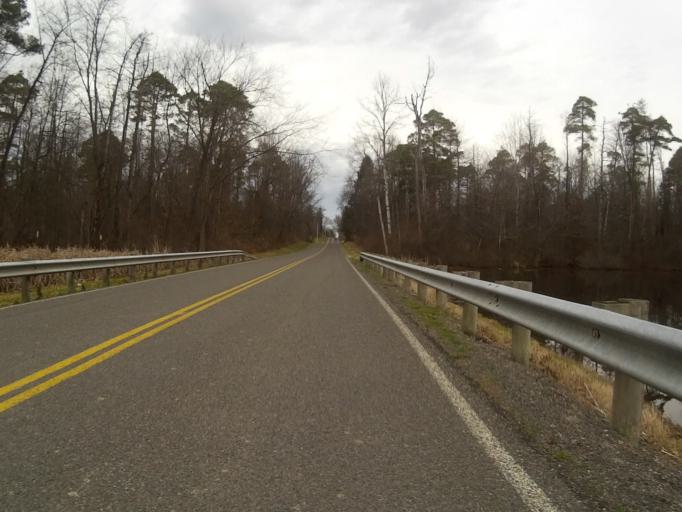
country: US
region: Ohio
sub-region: Portage County
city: Brimfield
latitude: 41.0635
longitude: -81.3288
